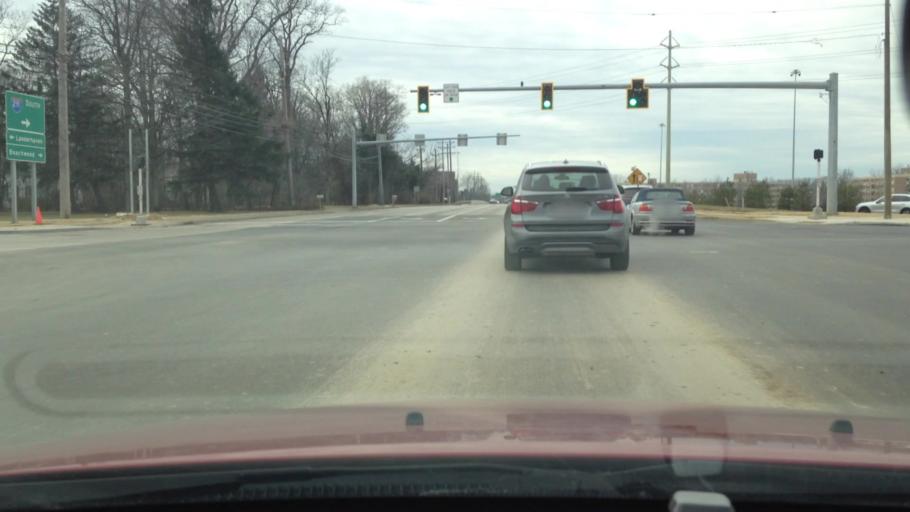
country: US
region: Ohio
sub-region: Cuyahoga County
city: Lyndhurst
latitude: 41.5012
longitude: -81.4763
